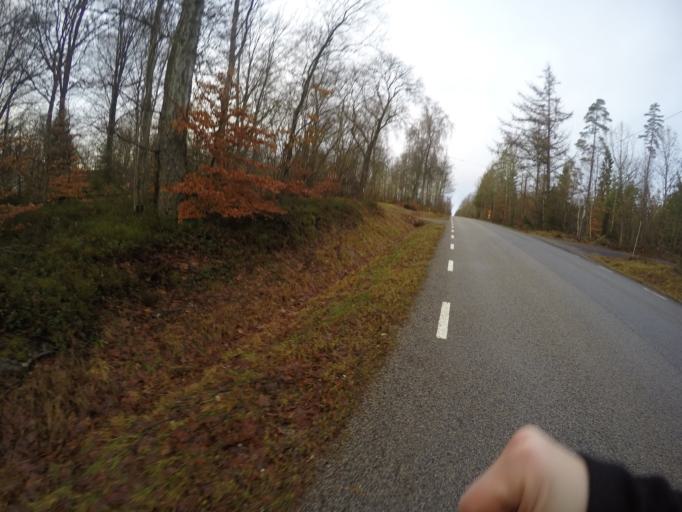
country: SE
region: Skane
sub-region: Osby Kommun
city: Lonsboda
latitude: 56.3789
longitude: 14.3442
